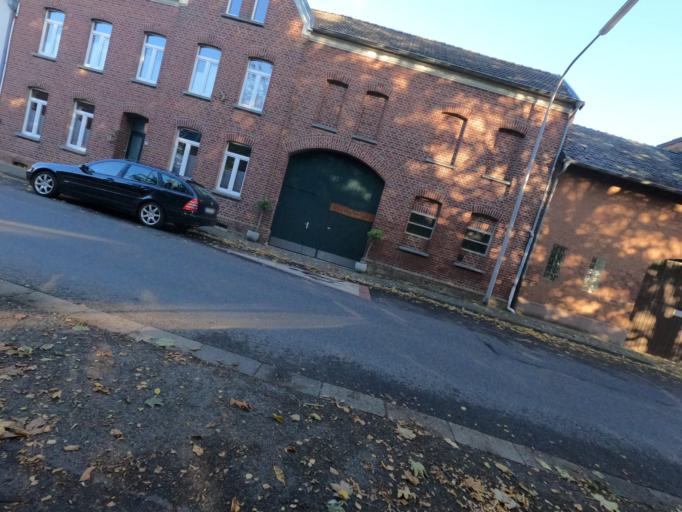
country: DE
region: North Rhine-Westphalia
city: Huckelhoven
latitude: 51.0281
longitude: 6.1752
